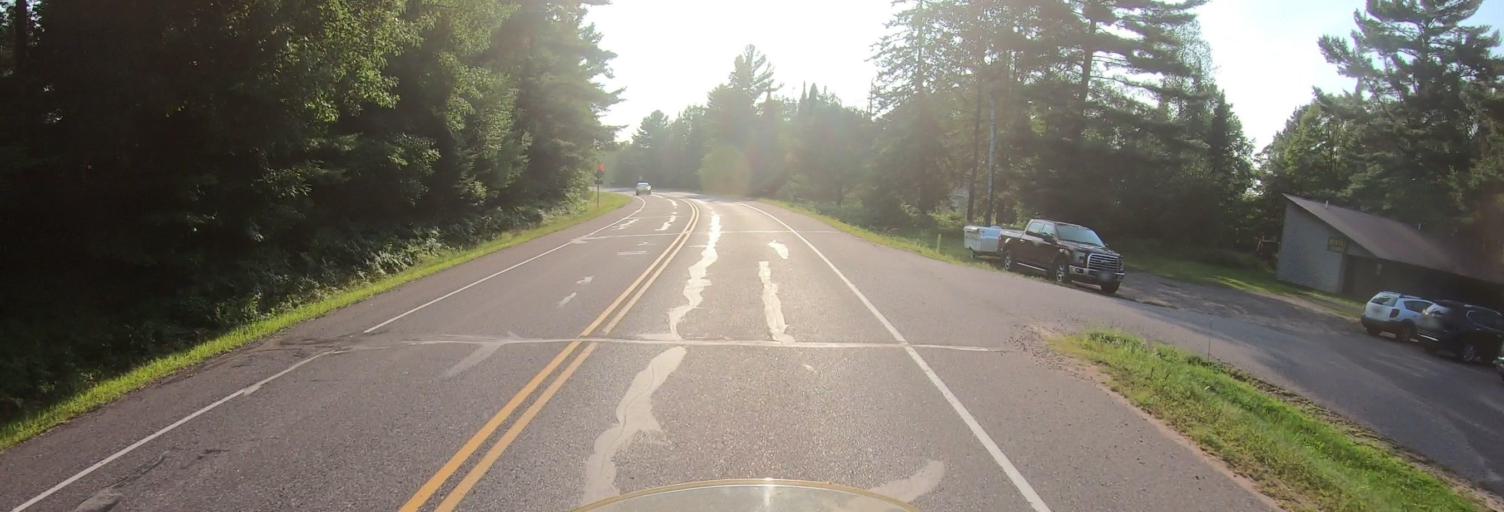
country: US
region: Wisconsin
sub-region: Ashland County
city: Ashland
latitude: 46.1674
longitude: -90.9125
